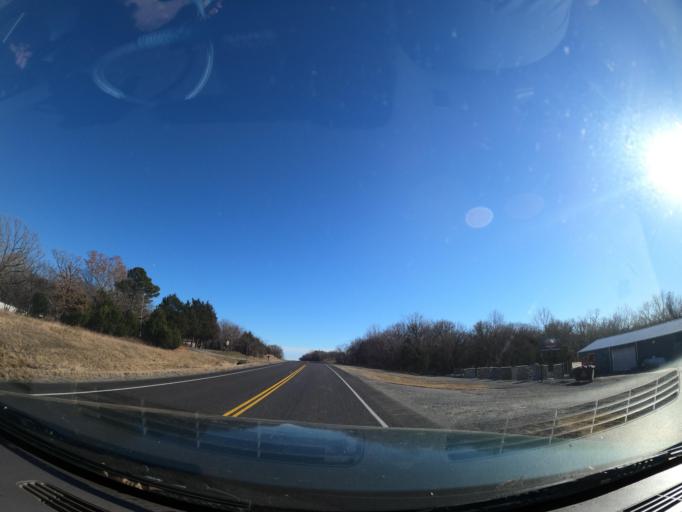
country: US
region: Oklahoma
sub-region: McIntosh County
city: Eufaula
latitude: 35.2540
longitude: -95.5753
